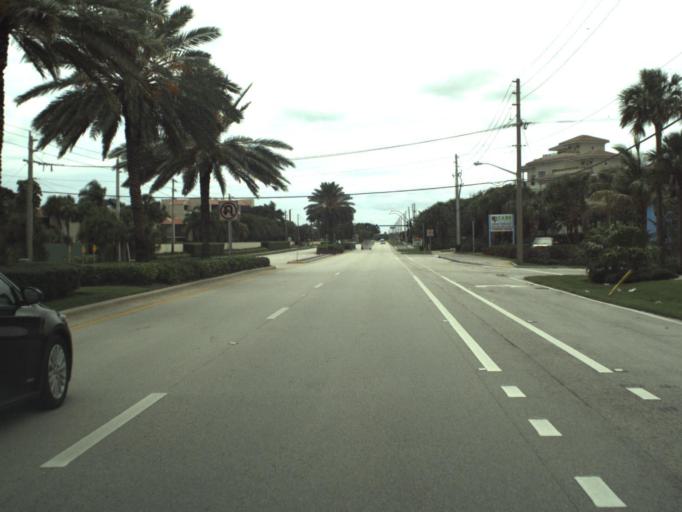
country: US
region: Florida
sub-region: Palm Beach County
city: Jupiter
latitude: 26.9219
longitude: -80.0747
